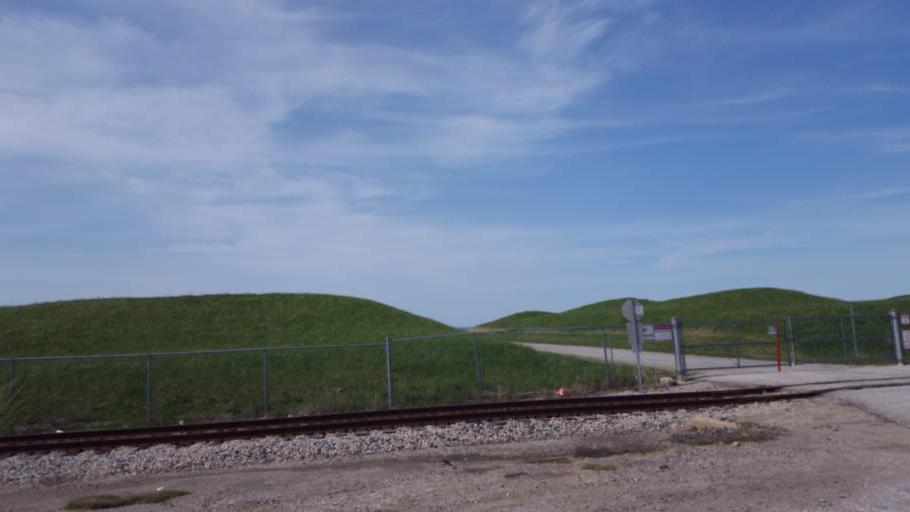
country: US
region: Ohio
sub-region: Lake County
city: Fairport Harbor
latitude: 41.7561
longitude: -81.2520
